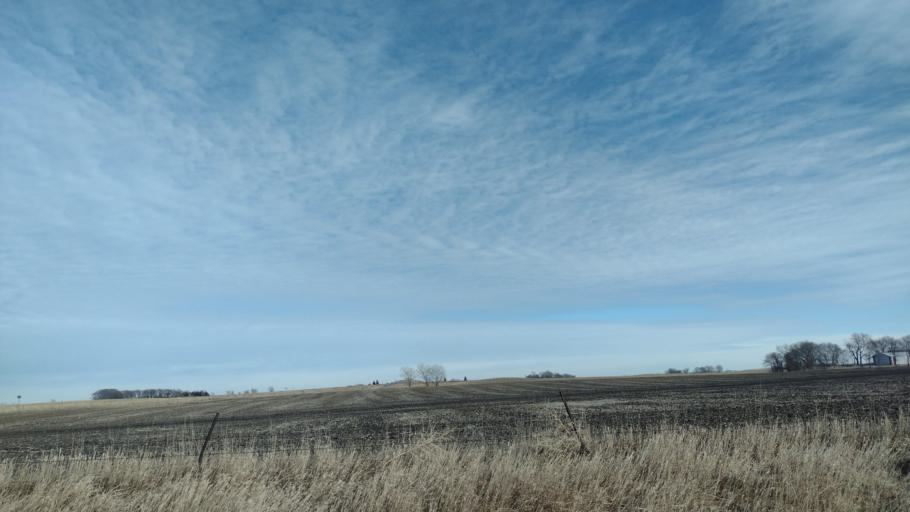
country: US
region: South Dakota
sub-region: Union County
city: Beresford
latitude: 42.9527
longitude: -96.8055
